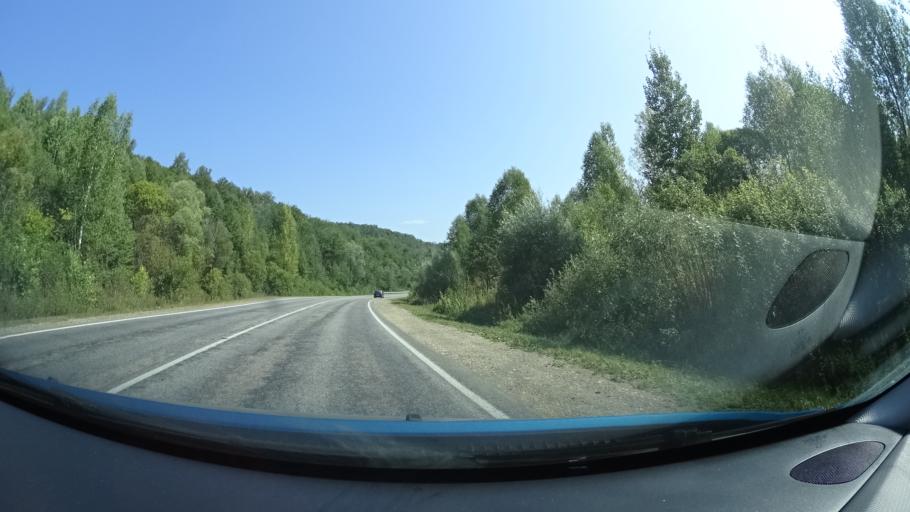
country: RU
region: Bashkortostan
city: Inzer
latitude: 54.3375
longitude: 57.1059
